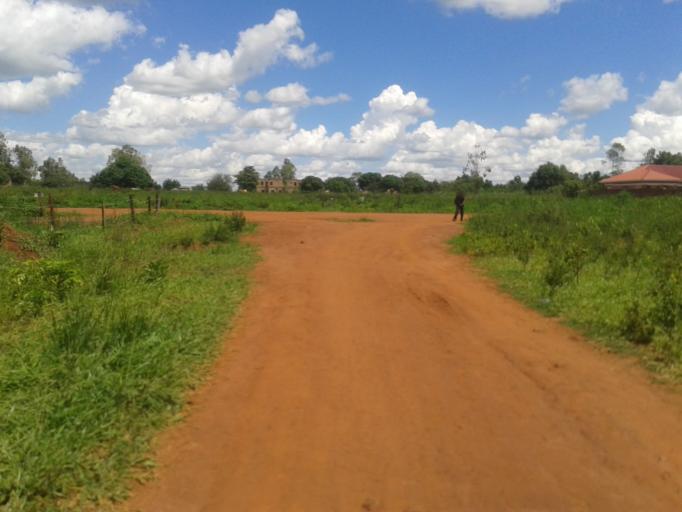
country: UG
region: Northern Region
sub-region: Gulu District
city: Gulu
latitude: 2.7595
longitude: 32.3203
